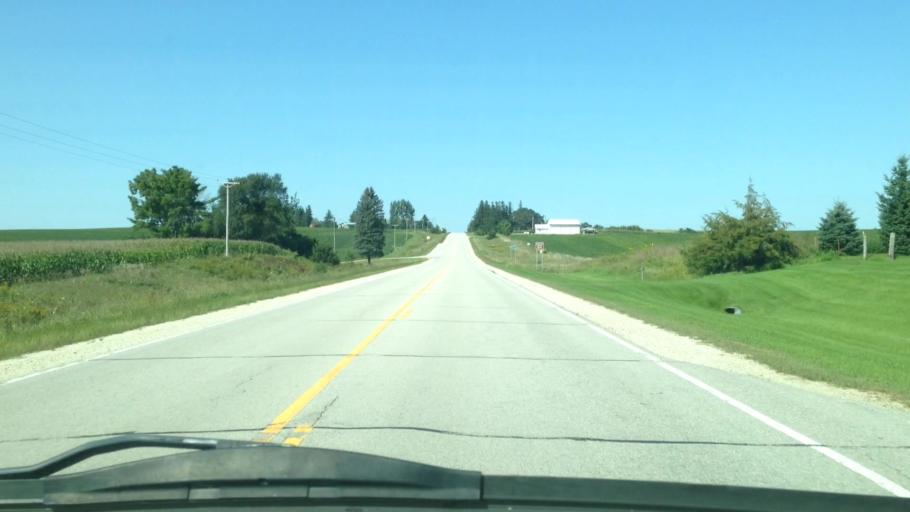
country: US
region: Minnesota
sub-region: Houston County
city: Spring Grove
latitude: 43.6143
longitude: -91.7904
